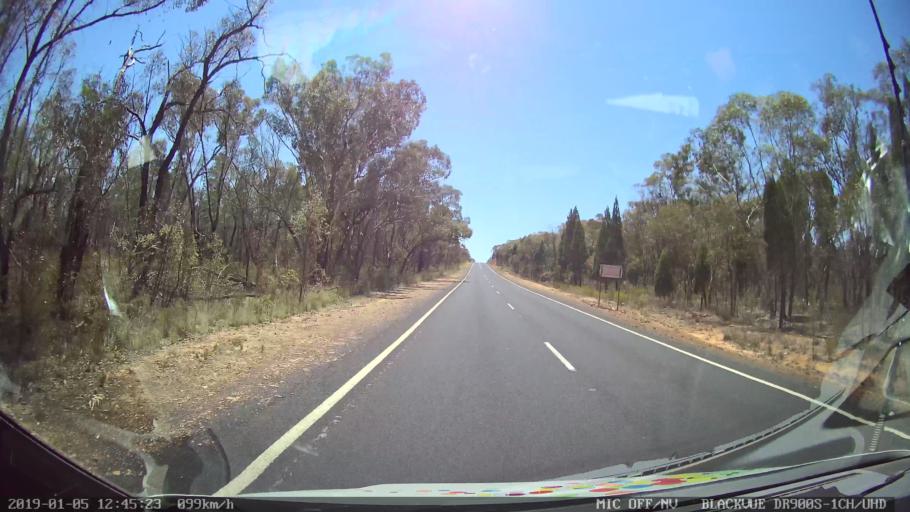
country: AU
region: New South Wales
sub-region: Warrumbungle Shire
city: Coonabarabran
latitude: -31.1283
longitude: 149.5493
